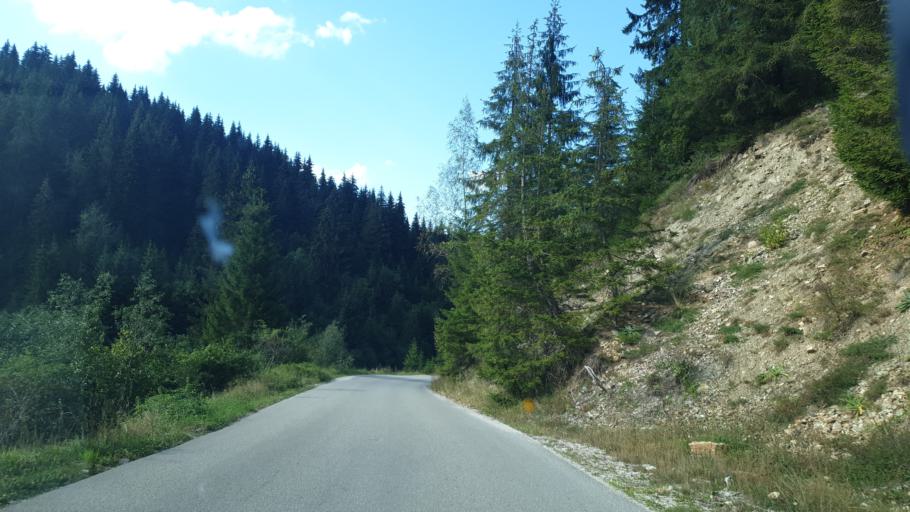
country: RS
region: Central Serbia
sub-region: Zlatiborski Okrug
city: Nova Varos
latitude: 43.4400
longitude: 19.8533
